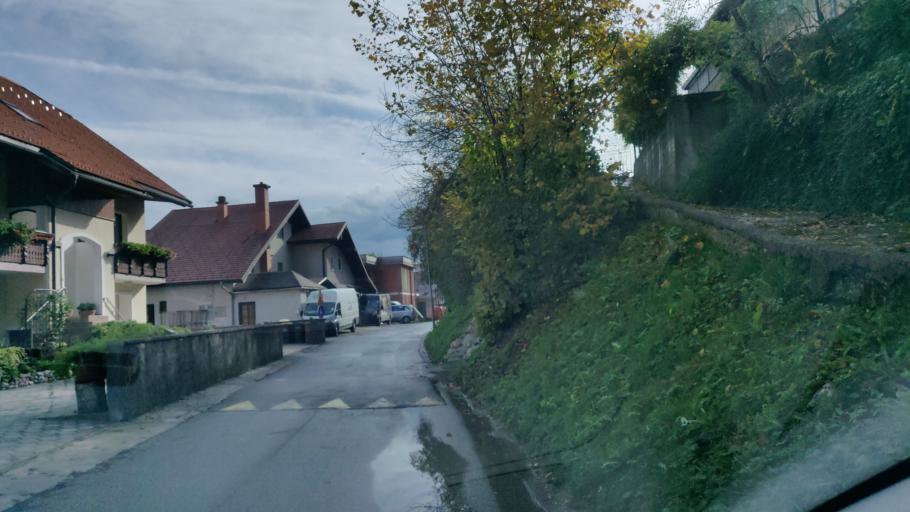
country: SI
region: Trzin
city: Trzin
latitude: 46.1331
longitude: 14.5607
